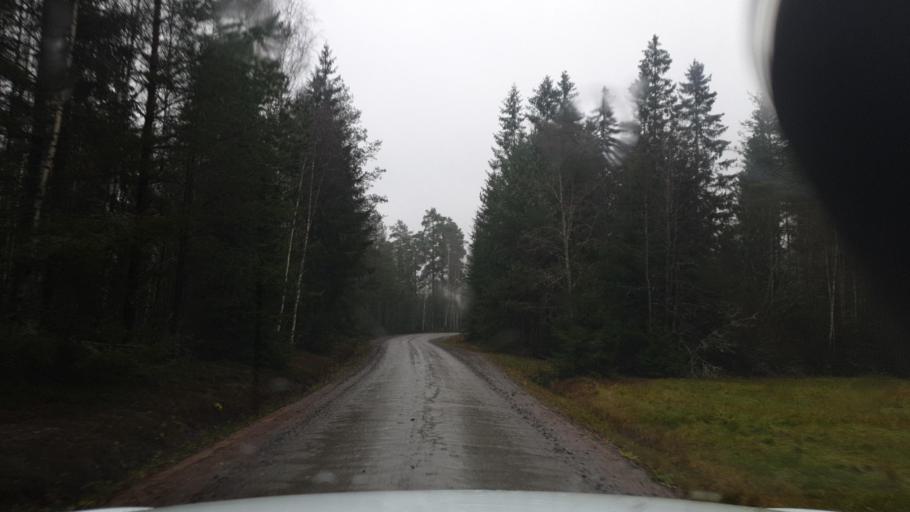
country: SE
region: Vaermland
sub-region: Karlstads Kommun
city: Edsvalla
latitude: 59.4882
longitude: 13.1642
